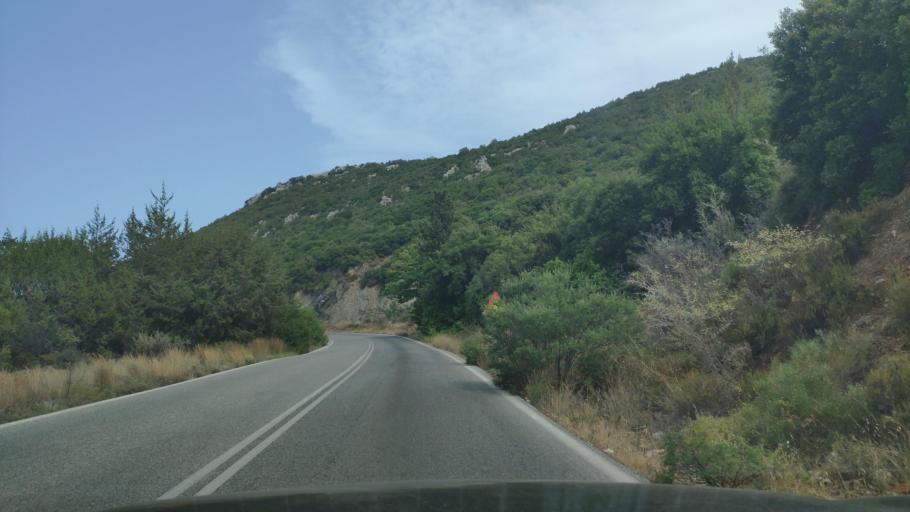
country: GR
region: Peloponnese
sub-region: Nomos Argolidos
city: Didyma
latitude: 37.5103
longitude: 23.1835
